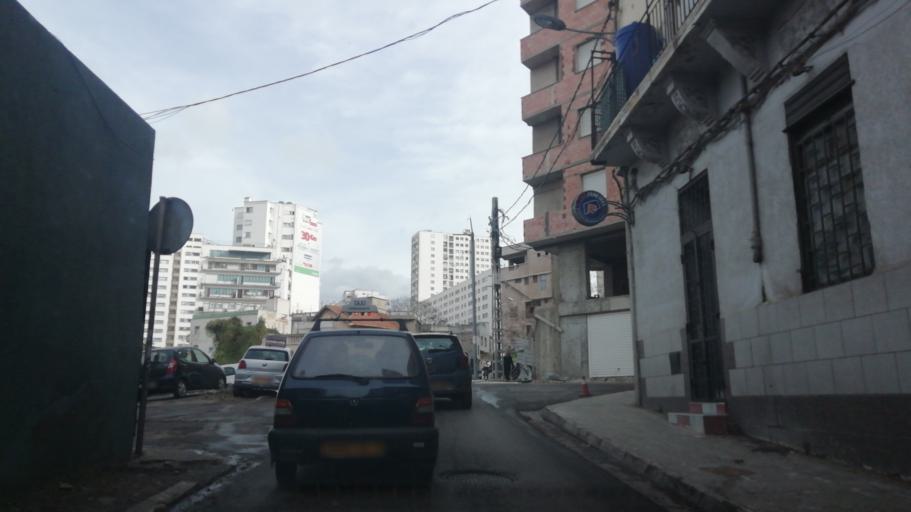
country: DZ
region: Oran
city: Oran
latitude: 35.7019
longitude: -0.6318
